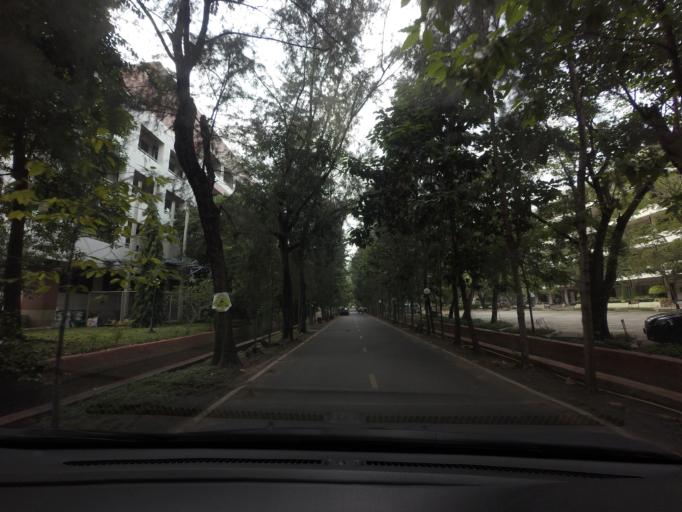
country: TH
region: Bangkok
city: Chatuchak
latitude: 13.8485
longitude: 100.5722
